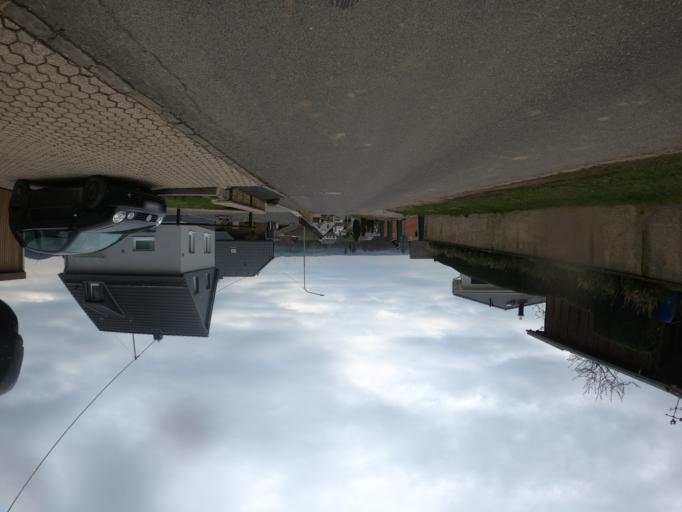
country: DE
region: North Rhine-Westphalia
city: Heimbach
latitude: 50.6715
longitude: 6.4247
